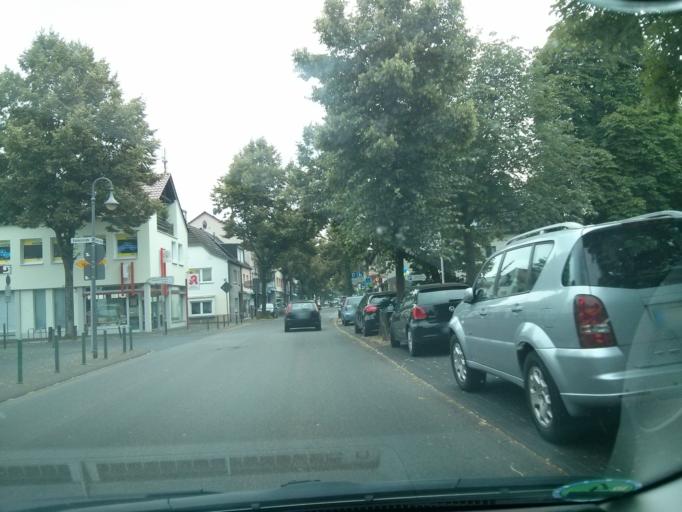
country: DE
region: North Rhine-Westphalia
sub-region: Regierungsbezirk Koln
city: Hennef
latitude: 50.7762
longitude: 7.2812
